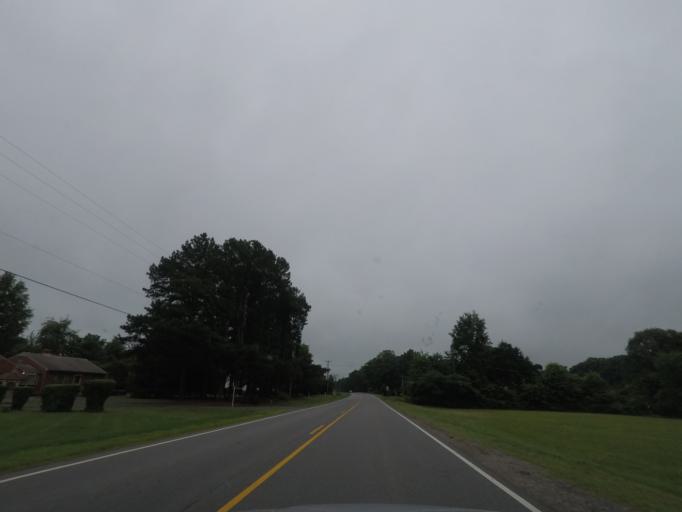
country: US
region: Virginia
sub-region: Fluvanna County
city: Weber City
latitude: 37.6399
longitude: -78.3596
